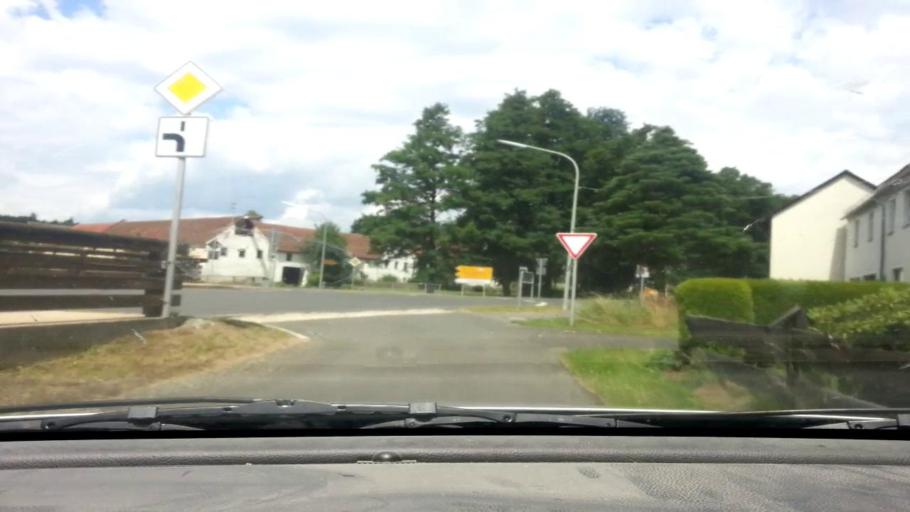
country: DE
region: Bavaria
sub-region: Upper Palatinate
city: Waldsassen
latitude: 50.0248
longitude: 12.3293
